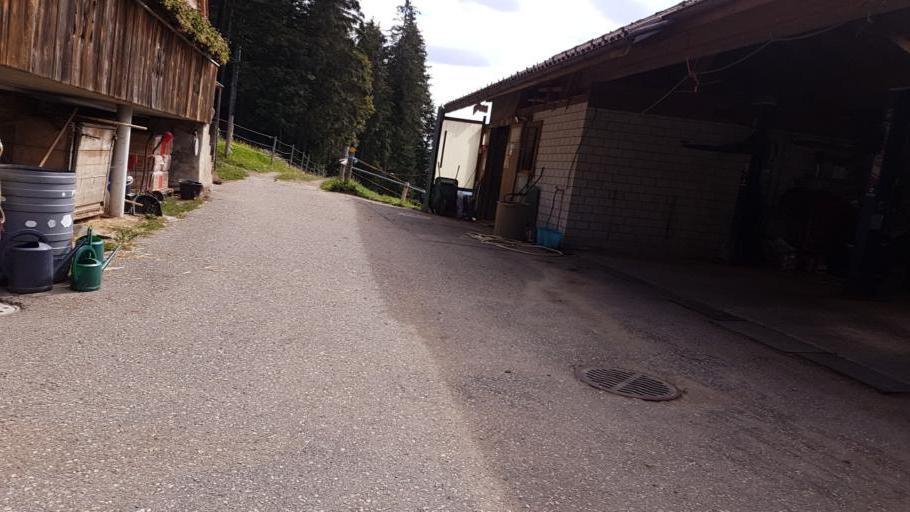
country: CH
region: Bern
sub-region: Bern-Mittelland District
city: Linden
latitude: 46.8628
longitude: 7.7011
